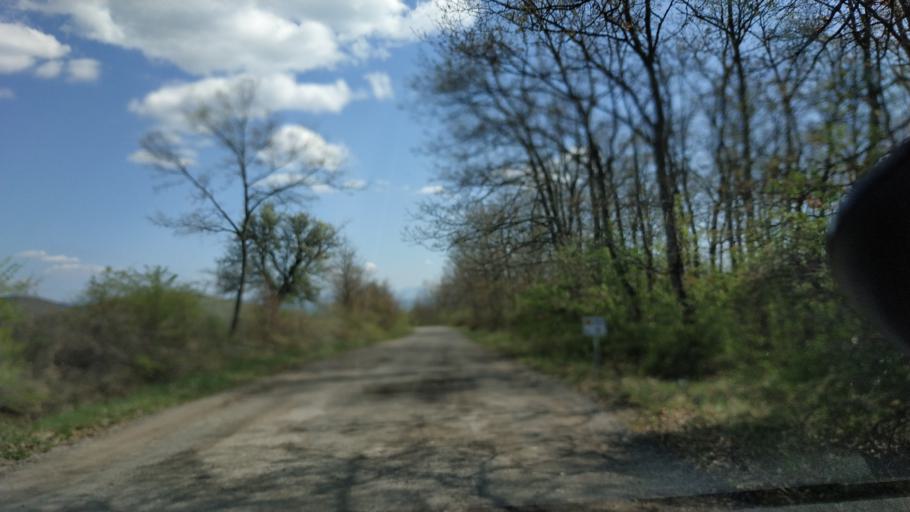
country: RS
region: Central Serbia
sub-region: Zajecarski Okrug
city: Soko Banja
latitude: 43.5451
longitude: 21.9010
